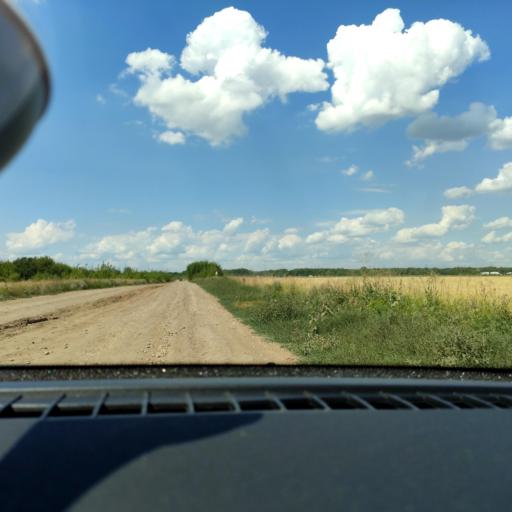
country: RU
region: Samara
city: Kinel'
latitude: 53.2568
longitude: 50.5289
